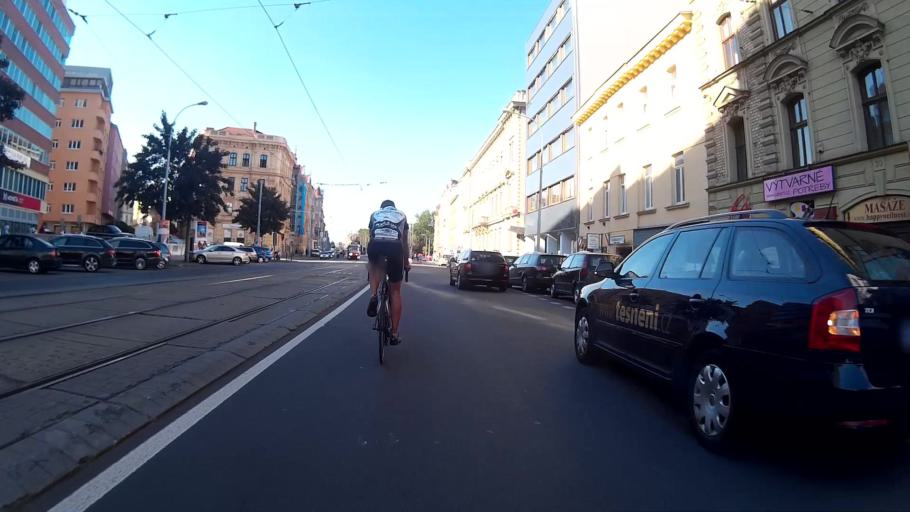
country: CZ
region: South Moravian
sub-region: Mesto Brno
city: Brno
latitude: 49.2025
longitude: 16.6073
